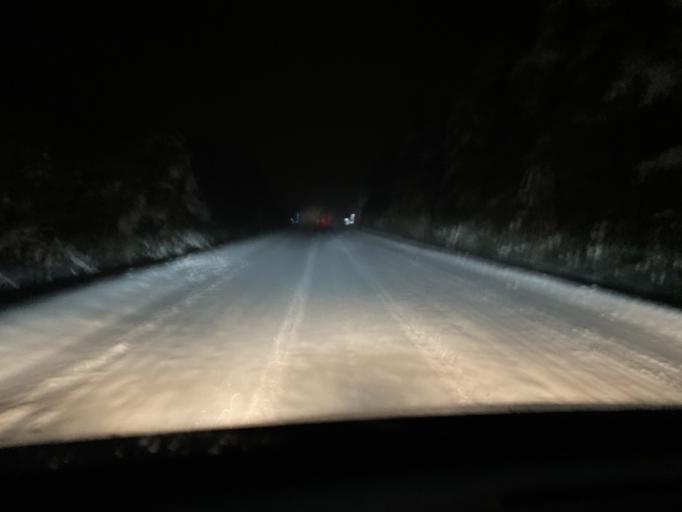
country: EE
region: Harju
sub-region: Kuusalu vald
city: Kuusalu
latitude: 59.4222
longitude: 25.3842
